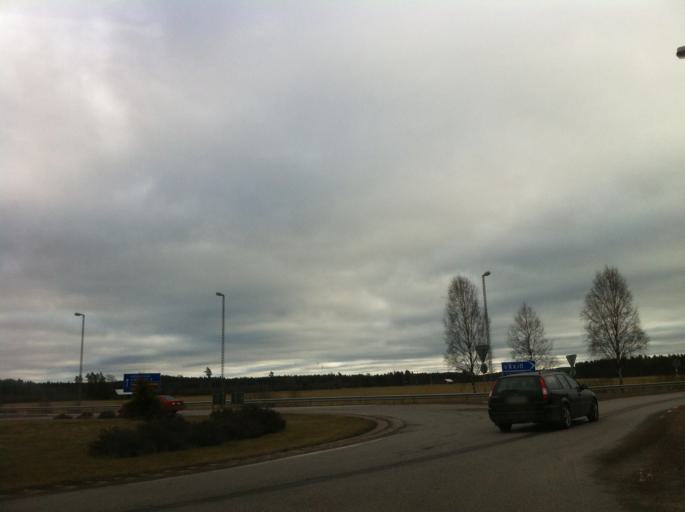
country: SE
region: Kalmar
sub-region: Vimmerby Kommun
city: Vimmerby
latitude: 57.6501
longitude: 15.8205
